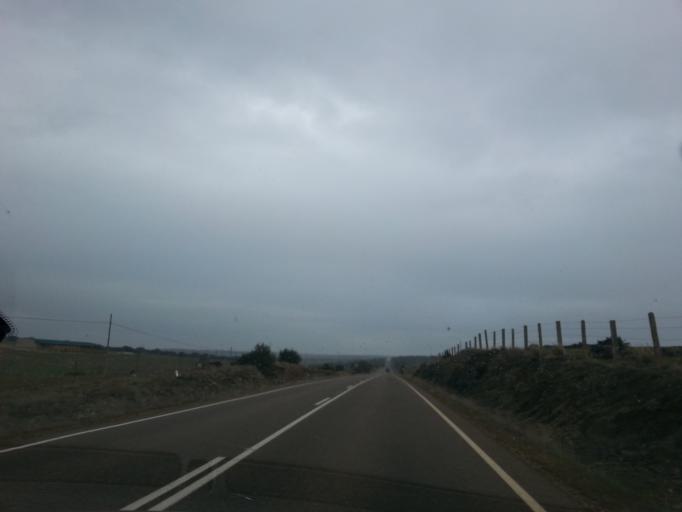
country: ES
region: Castille and Leon
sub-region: Provincia de Salamanca
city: Tamames
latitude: 40.6720
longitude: -6.0771
